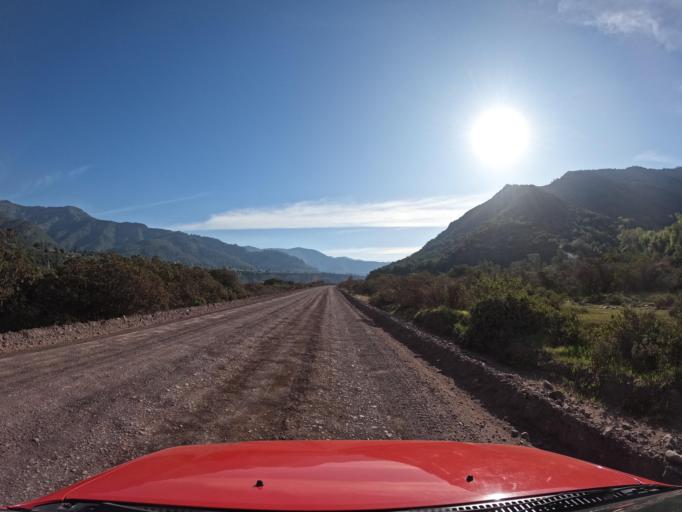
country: CL
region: Maule
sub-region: Provincia de Curico
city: Teno
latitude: -35.0018
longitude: -70.8309
